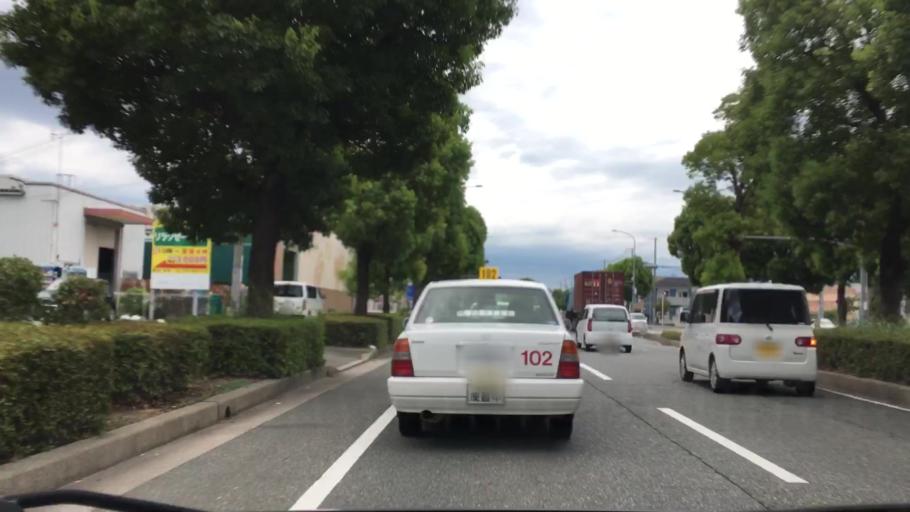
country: JP
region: Hyogo
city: Himeji
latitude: 34.8104
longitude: 134.6914
